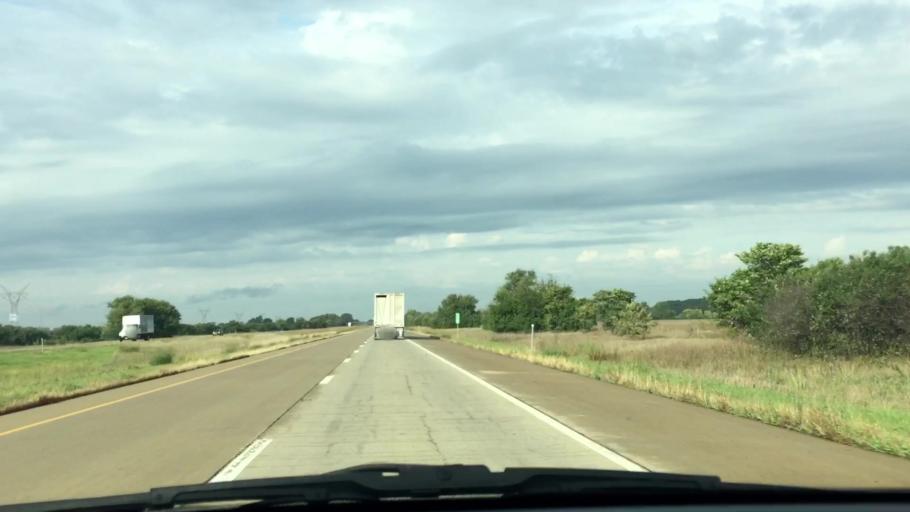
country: US
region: Illinois
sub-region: Whiteside County
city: Sterling
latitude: 41.7656
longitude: -89.8044
